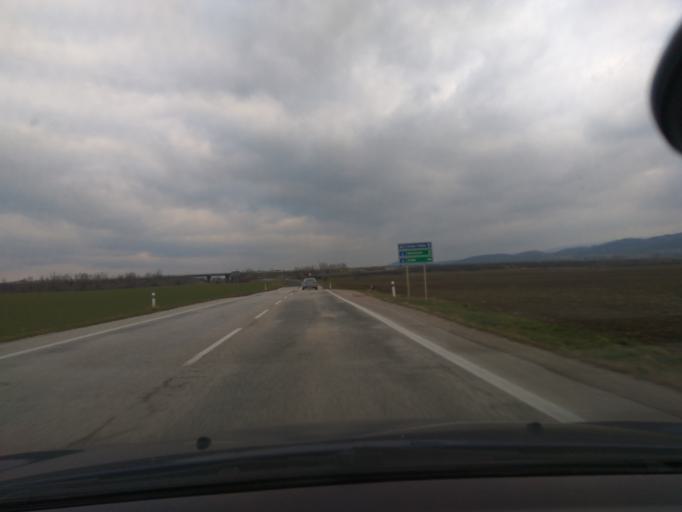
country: SK
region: Trnavsky
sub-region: Okres Trnava
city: Piestany
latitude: 48.6437
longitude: 17.8376
